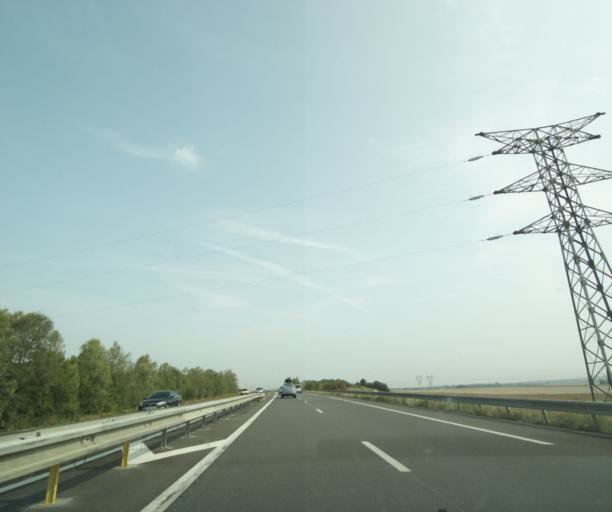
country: FR
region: Pays de la Loire
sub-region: Departement de la Sarthe
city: Arconnay
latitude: 48.3683
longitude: 0.1017
